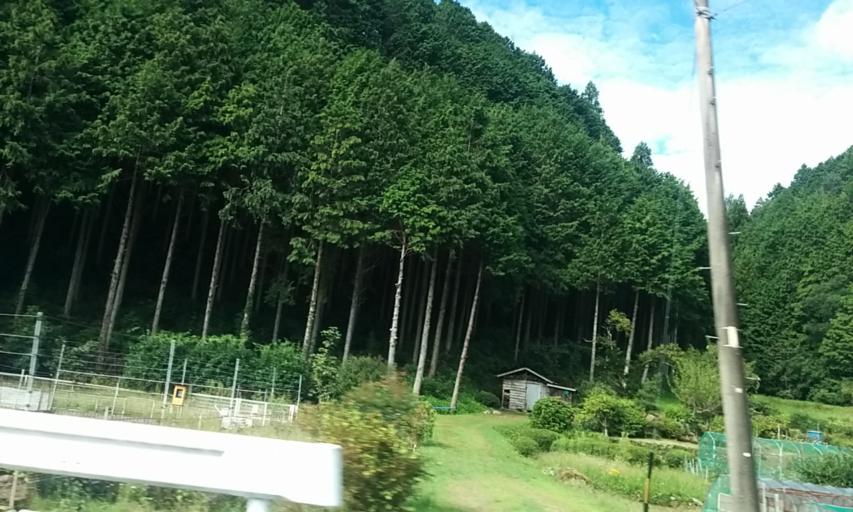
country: JP
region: Gifu
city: Minokamo
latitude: 35.5799
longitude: 137.0877
